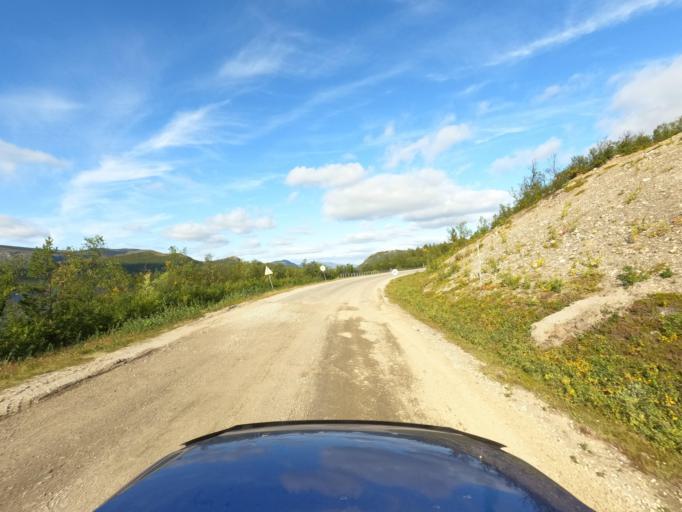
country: NO
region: Finnmark Fylke
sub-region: Porsanger
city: Lakselv
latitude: 69.8945
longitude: 24.9916
